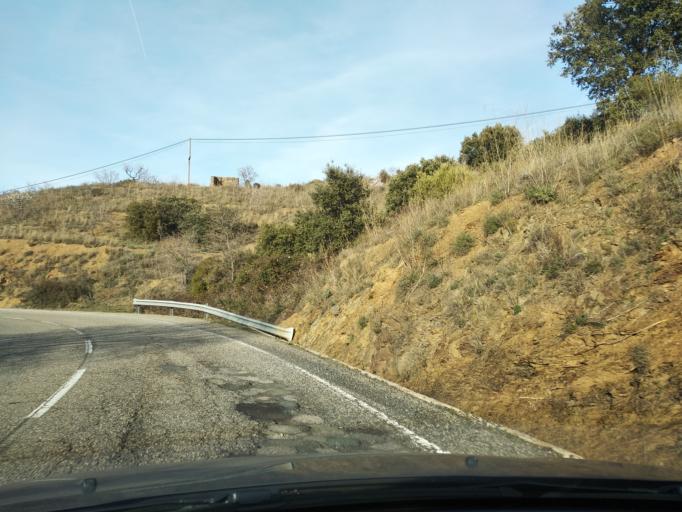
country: ES
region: Catalonia
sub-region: Provincia de Tarragona
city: Margalef
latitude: 41.2092
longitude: 0.7727
